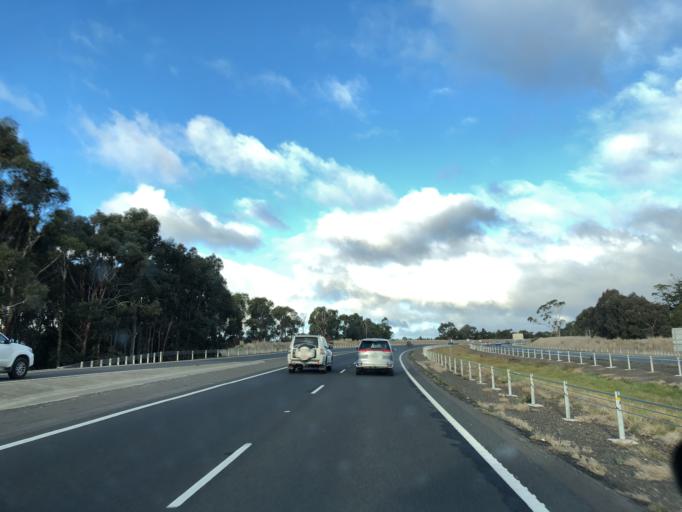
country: AU
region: Victoria
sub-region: Mount Alexander
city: Castlemaine
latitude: -37.2430
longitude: 144.4668
